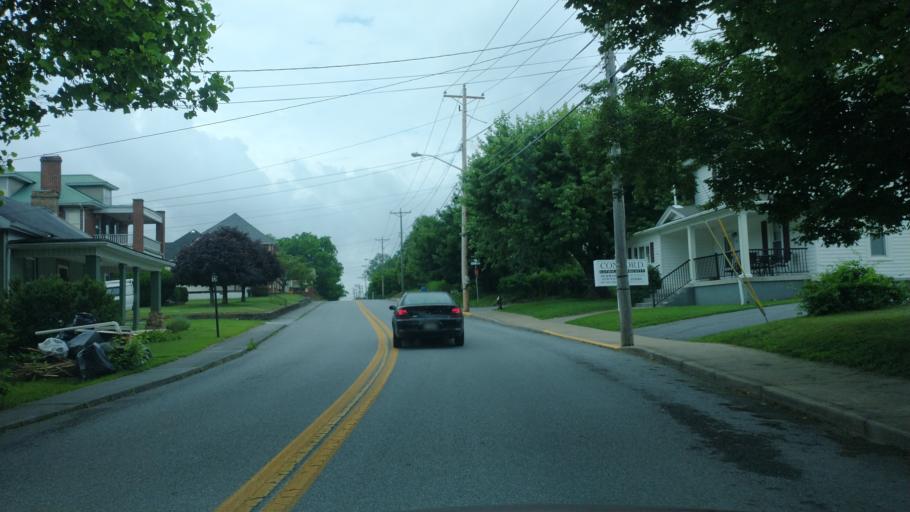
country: US
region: West Virginia
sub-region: Mercer County
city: Athens
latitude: 37.4232
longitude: -81.0113
